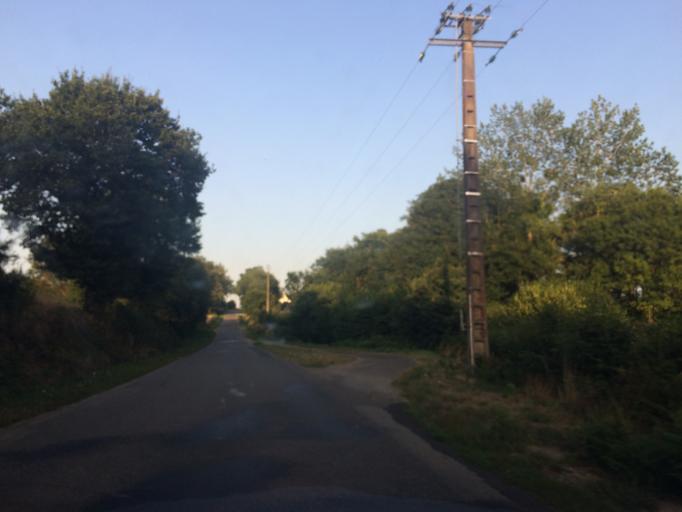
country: FR
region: Brittany
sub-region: Departement du Morbihan
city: Beganne
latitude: 47.6360
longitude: -2.2161
